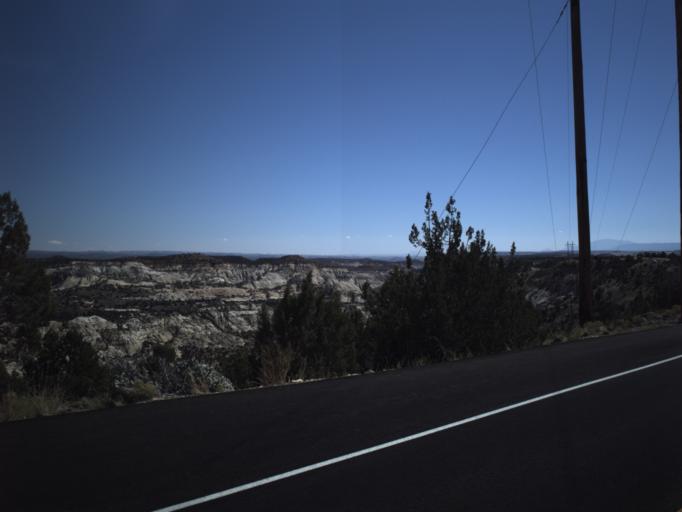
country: US
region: Utah
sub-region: Wayne County
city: Loa
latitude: 37.8407
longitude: -111.4217
